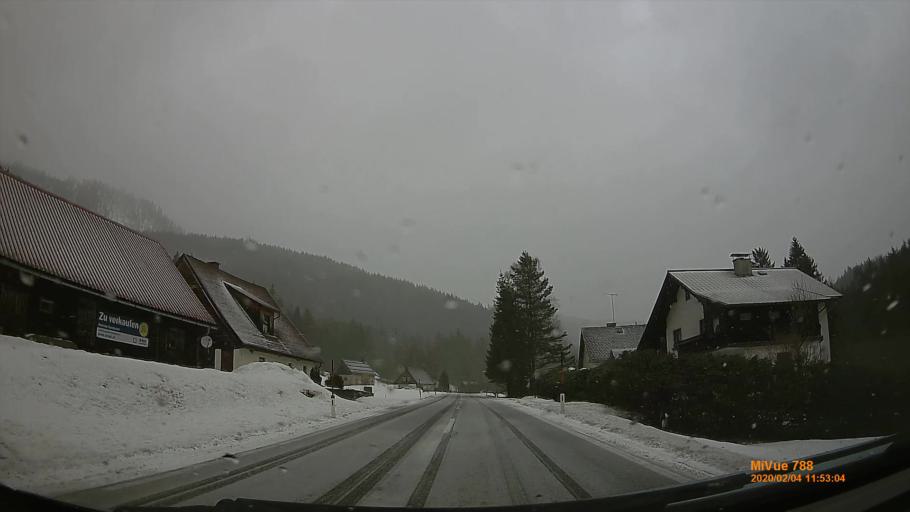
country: AT
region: Styria
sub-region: Politischer Bezirk Bruck-Muerzzuschlag
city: Muerzsteg
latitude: 47.7453
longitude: 15.4894
